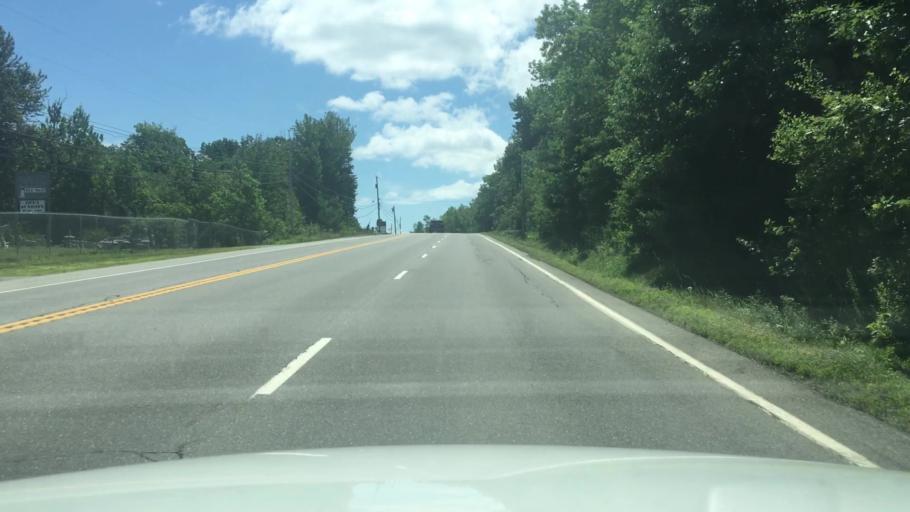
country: US
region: Maine
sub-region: Waldo County
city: Northport
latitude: 44.3630
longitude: -68.9770
